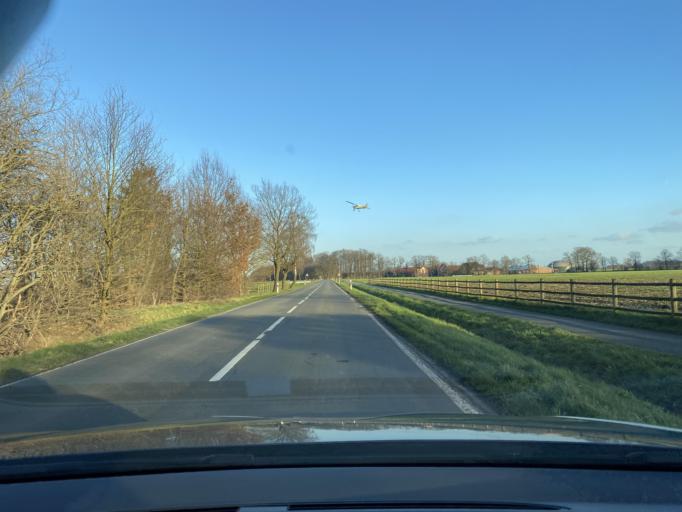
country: DE
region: North Rhine-Westphalia
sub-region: Regierungsbezirk Munster
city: Senden
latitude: 51.8249
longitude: 7.5148
